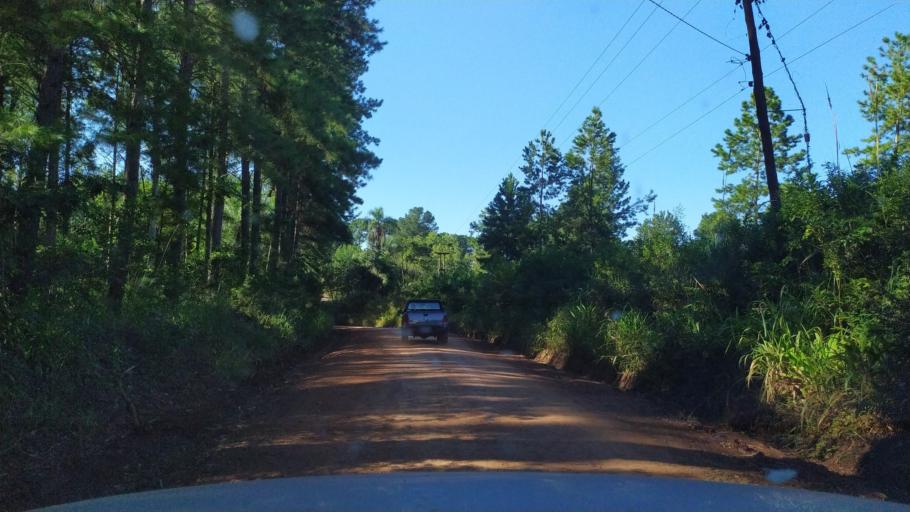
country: AR
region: Misiones
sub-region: Departamento de Montecarlo
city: Montecarlo
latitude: -26.6220
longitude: -54.6959
